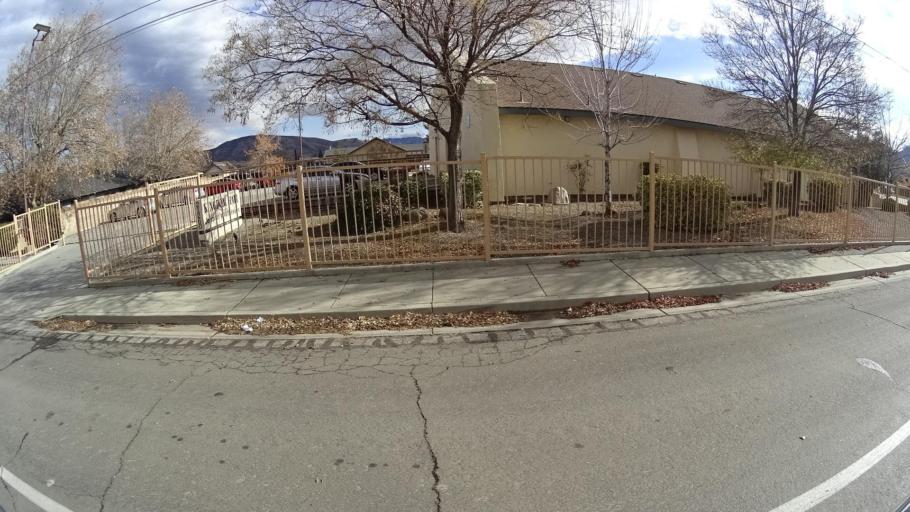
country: US
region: California
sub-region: Kern County
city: Golden Hills
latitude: 35.1284
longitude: -118.4859
